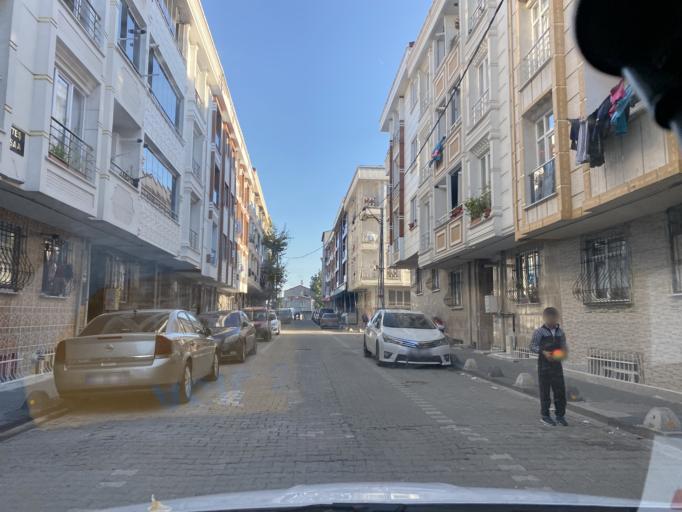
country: TR
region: Istanbul
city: Esenyurt
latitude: 41.0390
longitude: 28.6928
